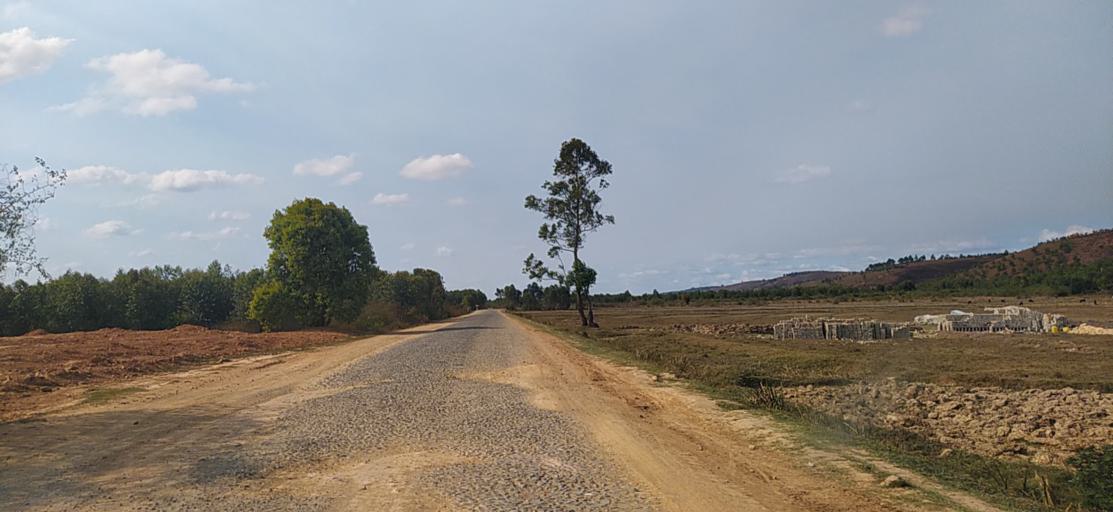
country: MG
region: Alaotra Mangoro
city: Moramanga
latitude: -18.6911
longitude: 48.2712
